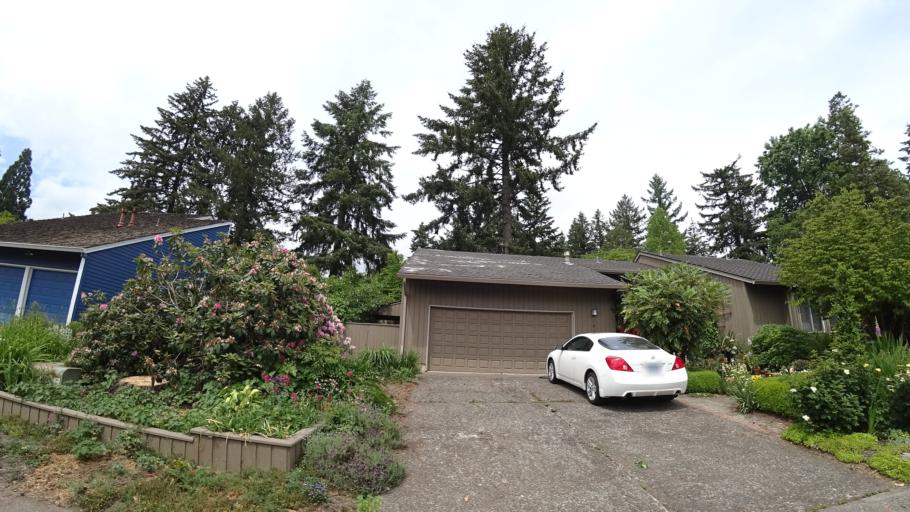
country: US
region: Oregon
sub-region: Washington County
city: Garden Home-Whitford
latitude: 45.4583
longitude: -122.7700
